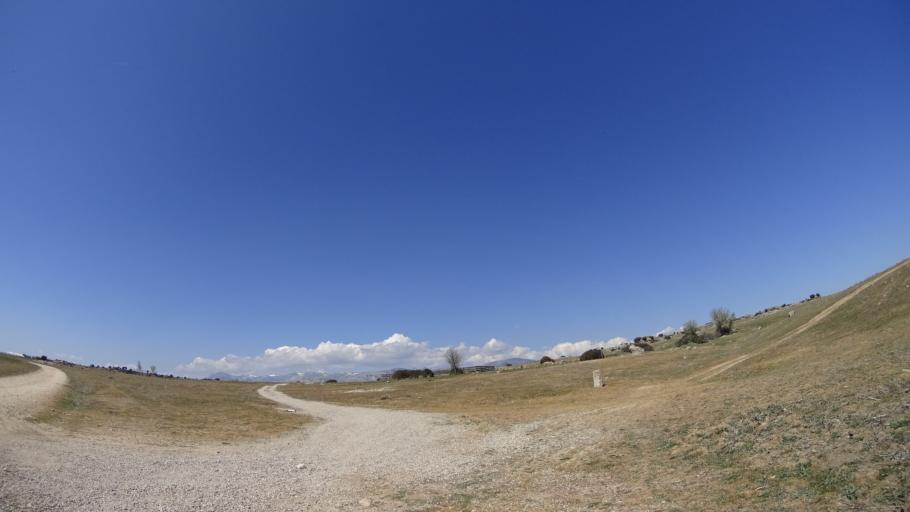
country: ES
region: Madrid
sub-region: Provincia de Madrid
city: Colmenar Viejo
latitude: 40.6998
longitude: -3.7499
